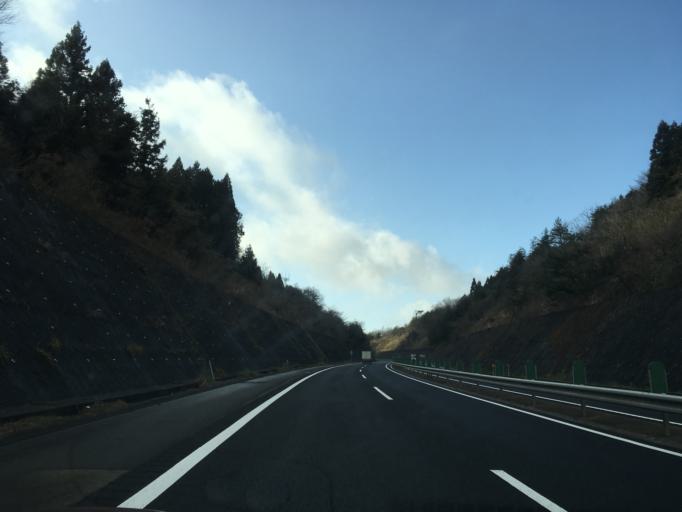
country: JP
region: Miyagi
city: Okawara
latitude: 38.1501
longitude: 140.6986
